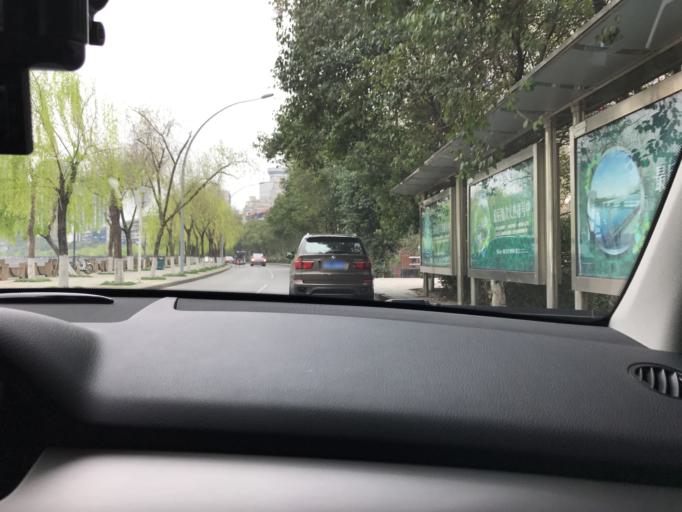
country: CN
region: Sichuan
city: Mianyang
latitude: 31.4597
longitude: 104.7457
